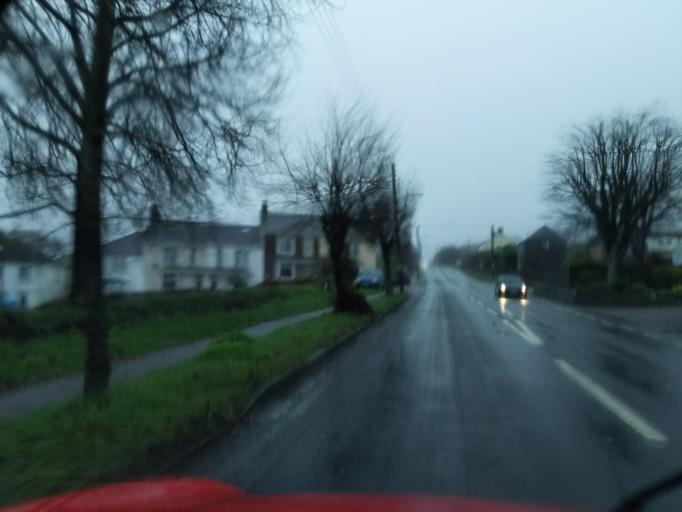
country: GB
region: England
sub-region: Cornwall
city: Callington
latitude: 50.5108
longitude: -4.3139
